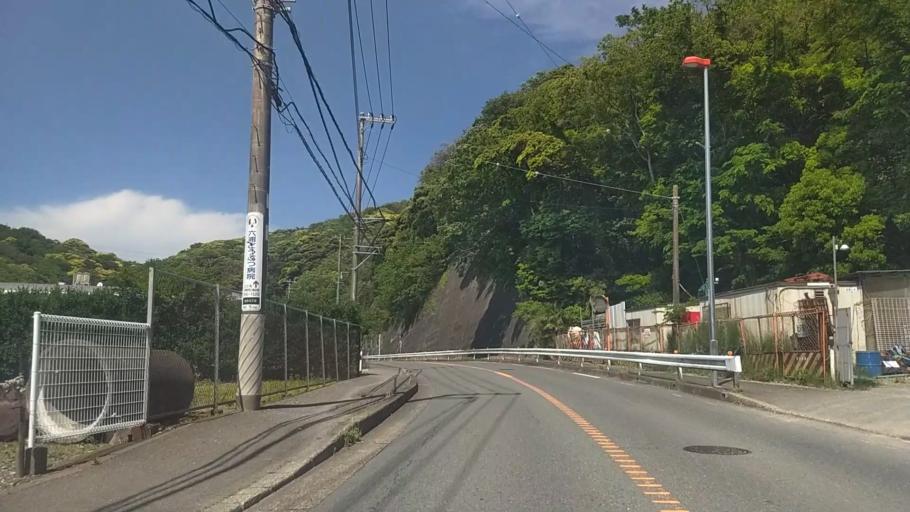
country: JP
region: Kanagawa
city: Zushi
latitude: 35.3111
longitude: 139.6003
